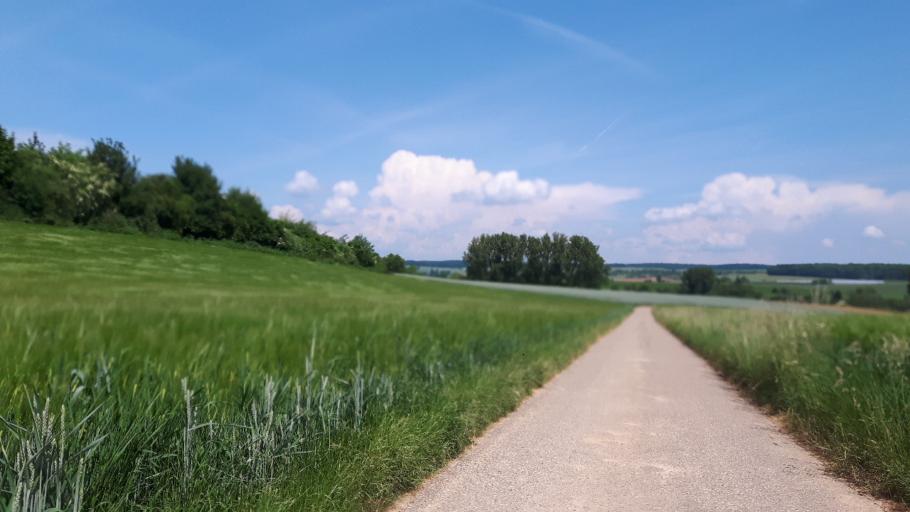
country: DE
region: Baden-Wuerttemberg
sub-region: Regierungsbezirk Stuttgart
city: Neuenstadt am Kocher
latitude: 49.2360
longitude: 9.3127
